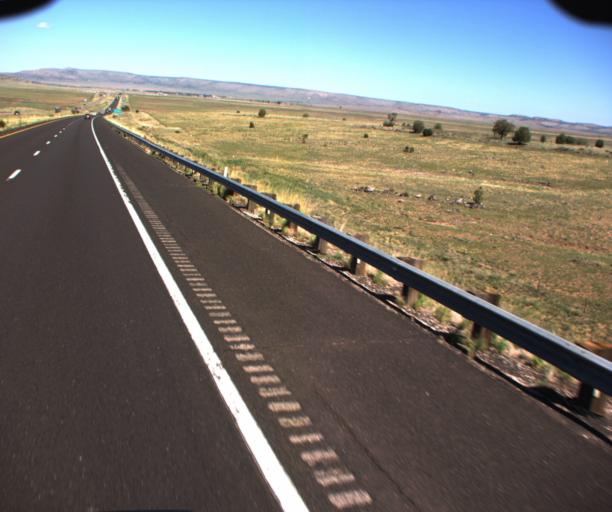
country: US
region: Arizona
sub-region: Yavapai County
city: Paulden
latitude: 35.2938
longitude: -112.8263
